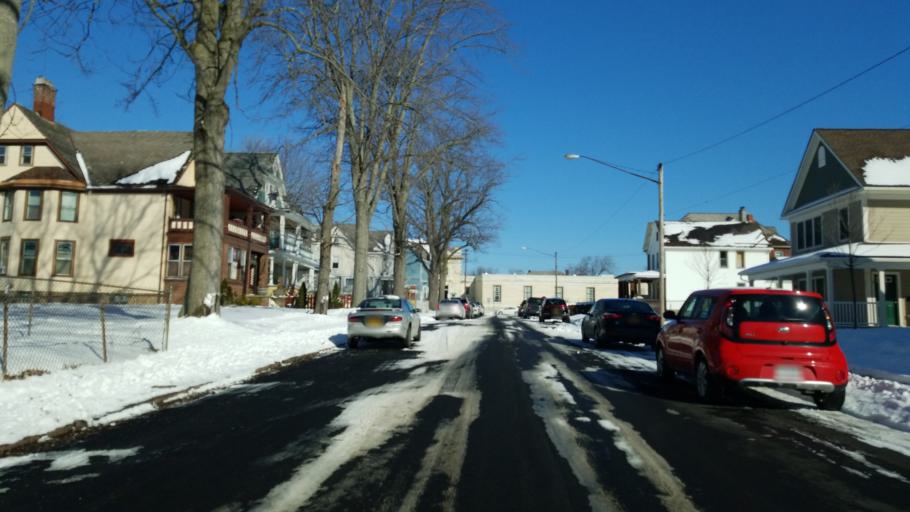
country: US
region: New York
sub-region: Niagara County
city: Niagara Falls
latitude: 43.0918
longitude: -79.0569
